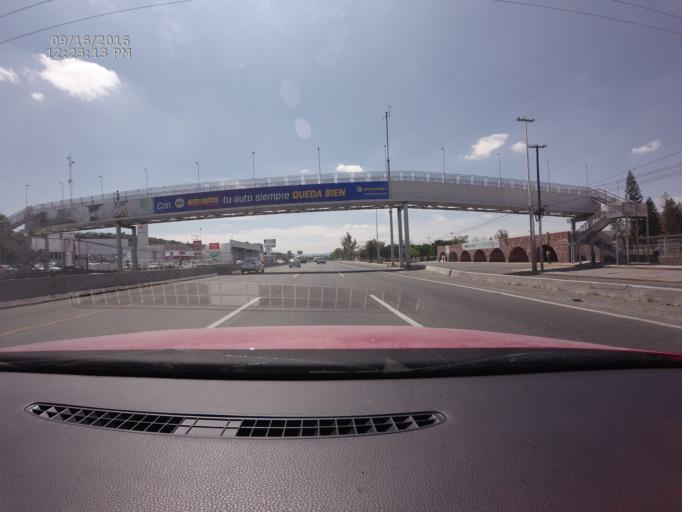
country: MX
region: Queretaro
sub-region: Queretaro
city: Sergio Villasenor
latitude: 20.6299
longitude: -100.4259
